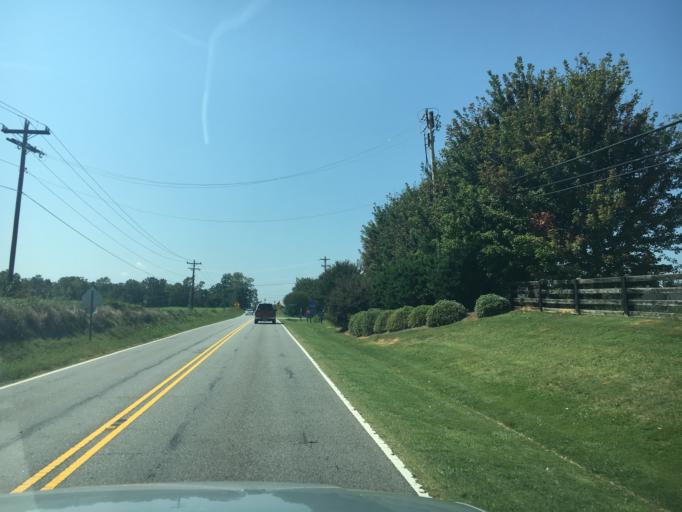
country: US
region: South Carolina
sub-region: Anderson County
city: Centerville
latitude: 34.5256
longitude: -82.7130
